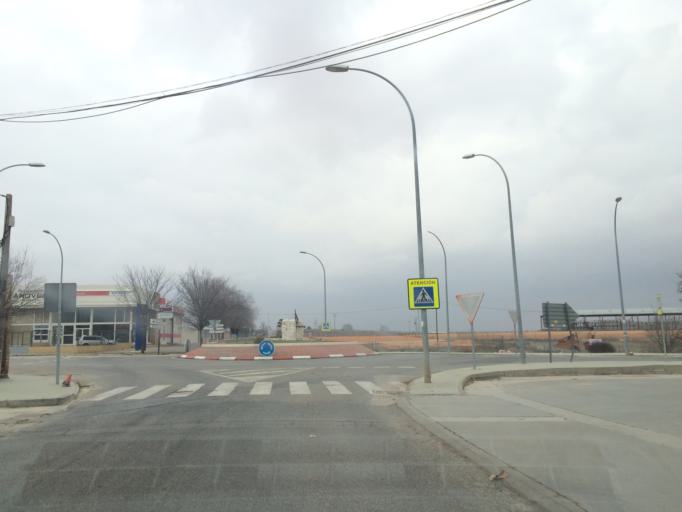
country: ES
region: Castille-La Mancha
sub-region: Province of Toledo
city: Madridejos
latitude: 39.4757
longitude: -3.5273
